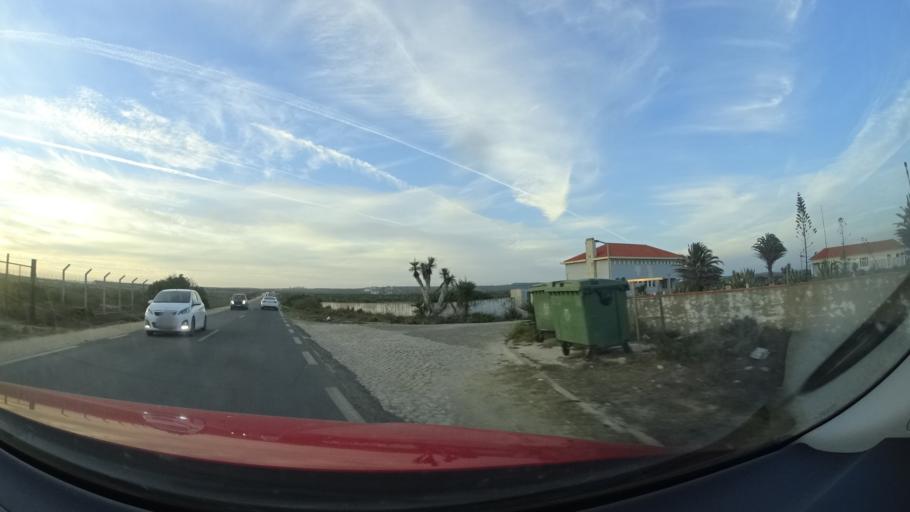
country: PT
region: Faro
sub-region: Vila do Bispo
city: Sagres
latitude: 37.0117
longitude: -8.9510
